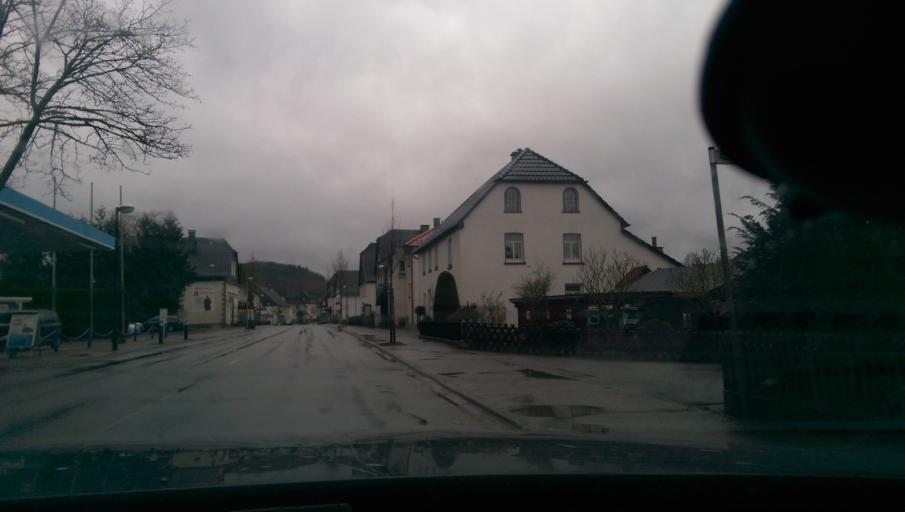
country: DE
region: North Rhine-Westphalia
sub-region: Regierungsbezirk Arnsberg
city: Sundern
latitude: 51.2852
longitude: 7.9546
